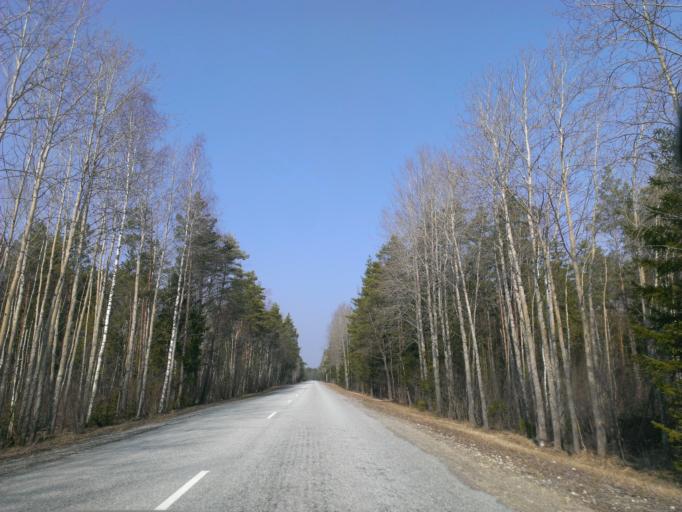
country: EE
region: Saare
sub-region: Kuressaare linn
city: Kuressaare
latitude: 58.3514
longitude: 22.6766
